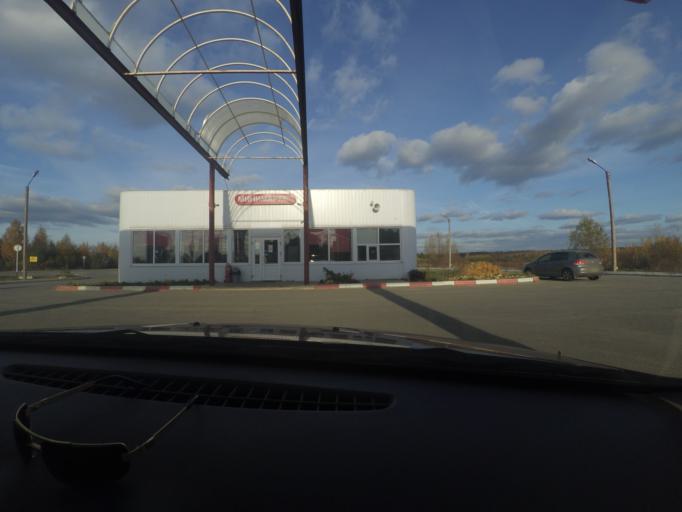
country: RU
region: Vladimir
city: Melenki
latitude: 55.3245
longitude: 41.6522
